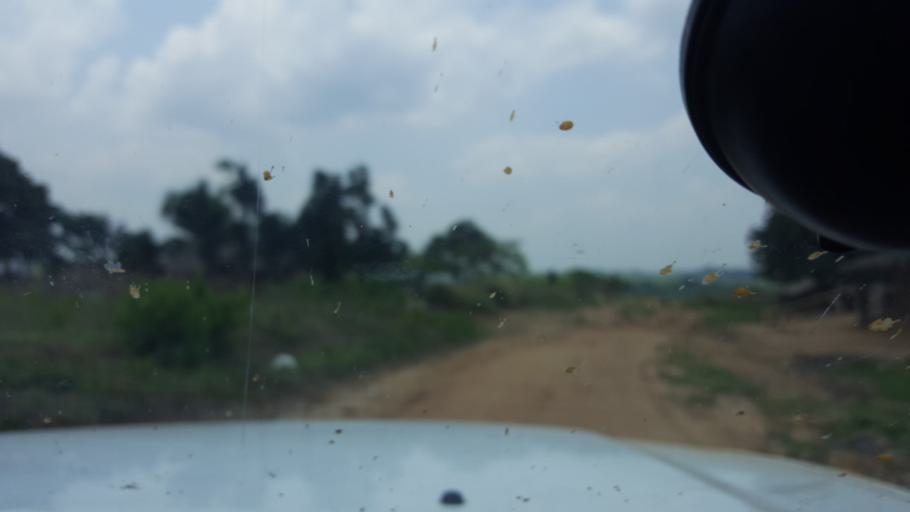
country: CD
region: Bandundu
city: Mushie
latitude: -3.7423
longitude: 16.6532
